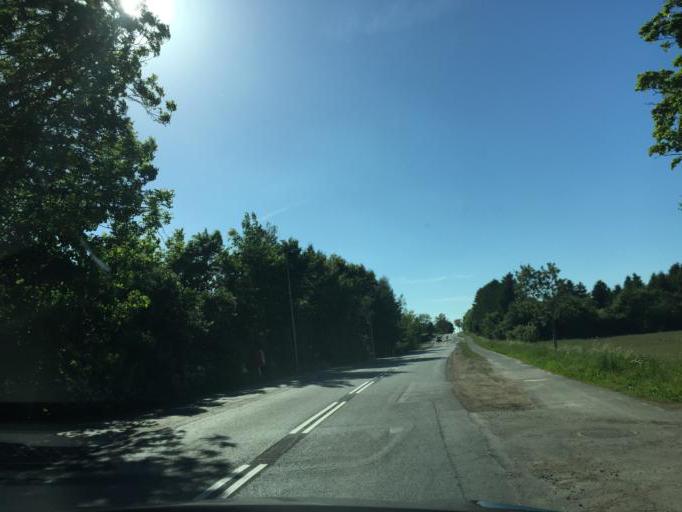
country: DK
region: Zealand
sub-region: Koge Kommune
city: Bjaeverskov
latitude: 55.4279
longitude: 11.9871
